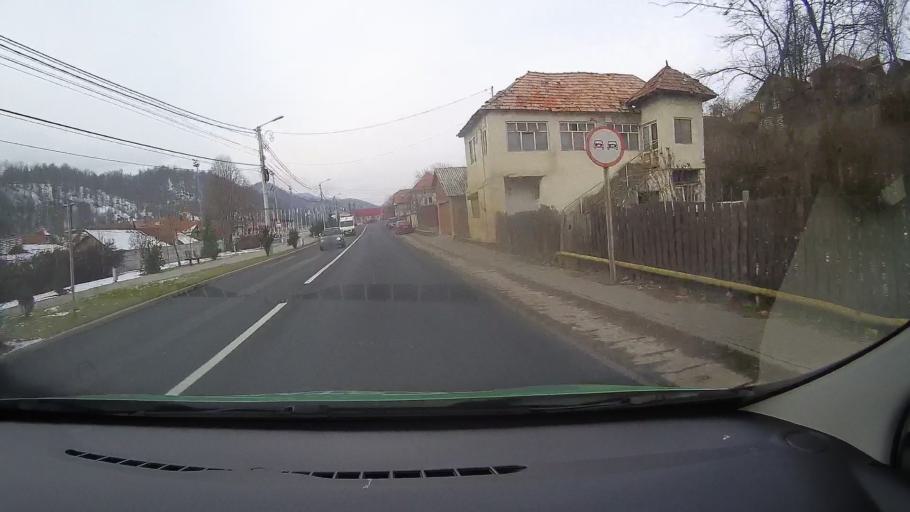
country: RO
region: Alba
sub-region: Oras Zlatna
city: Zlatna
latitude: 46.1147
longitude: 23.2146
